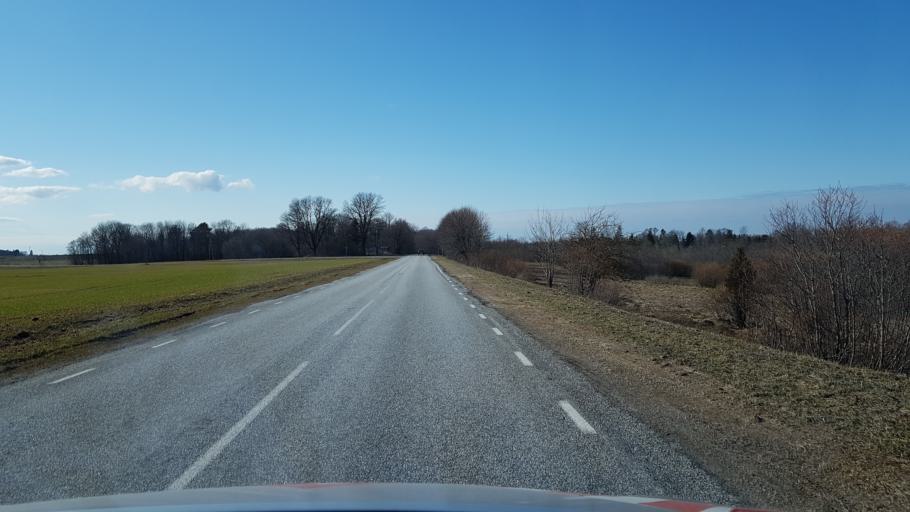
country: EE
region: Laeaene-Virumaa
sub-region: Haljala vald
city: Haljala
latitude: 59.4743
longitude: 26.1658
